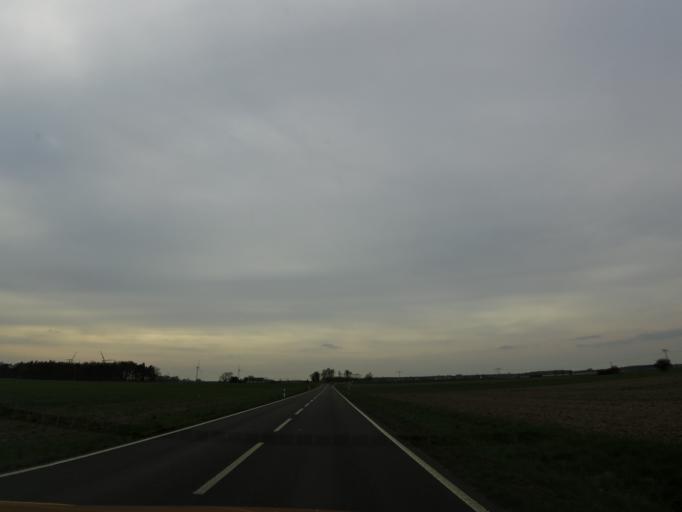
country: DE
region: Brandenburg
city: Tauche
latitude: 52.1742
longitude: 14.1899
